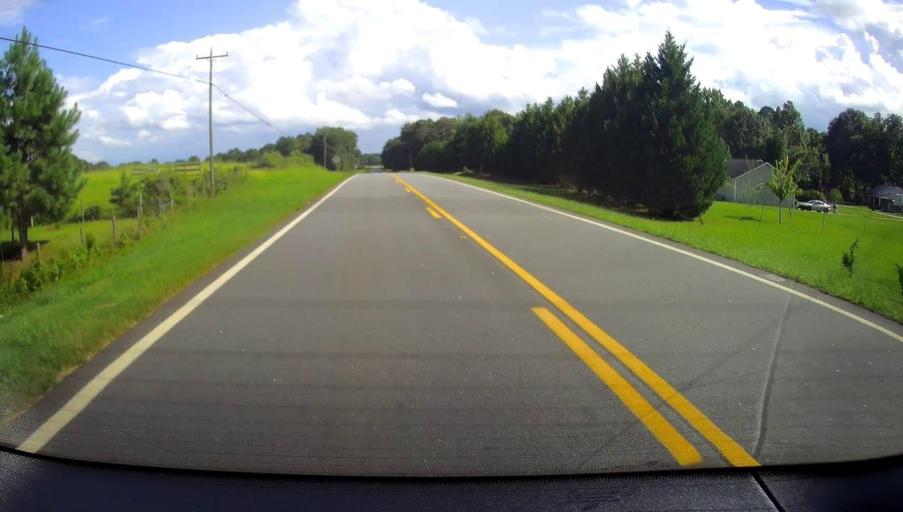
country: US
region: Georgia
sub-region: Upson County
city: Hannahs Mill
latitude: 32.9102
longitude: -84.4264
